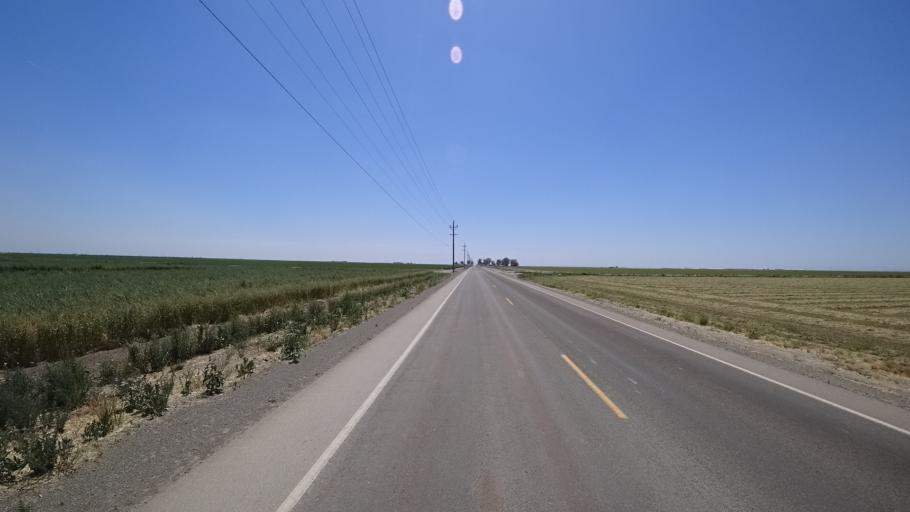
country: US
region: California
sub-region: Kings County
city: Corcoran
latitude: 36.1537
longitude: -119.6457
